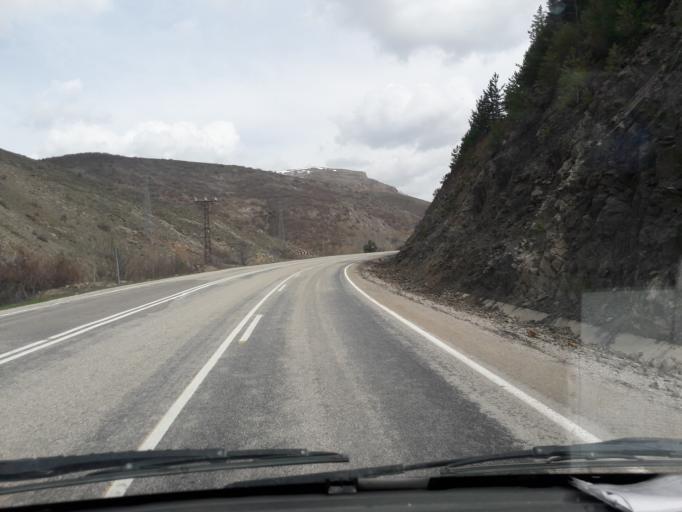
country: TR
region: Gumushane
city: Kelkit
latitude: 40.2892
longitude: 39.4863
